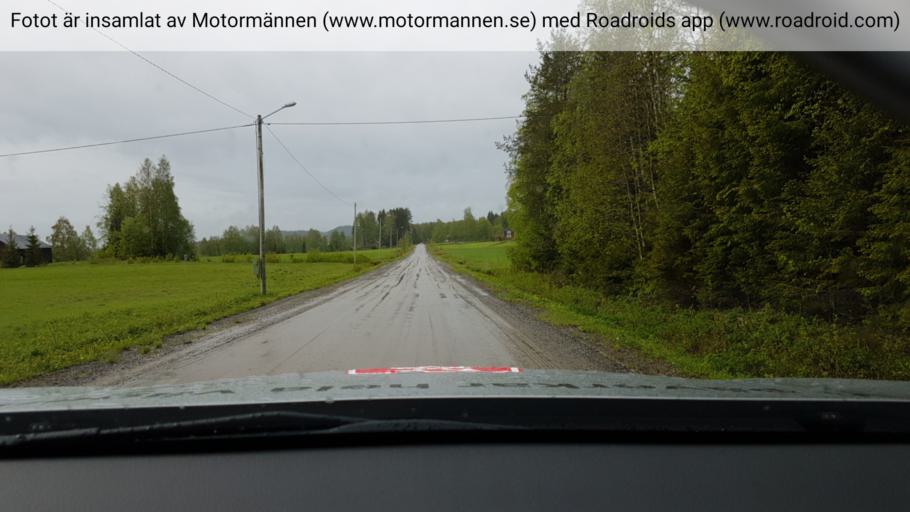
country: SE
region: Vaesterbotten
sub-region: Vannas Kommun
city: Vaennaes
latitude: 63.8342
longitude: 19.6320
